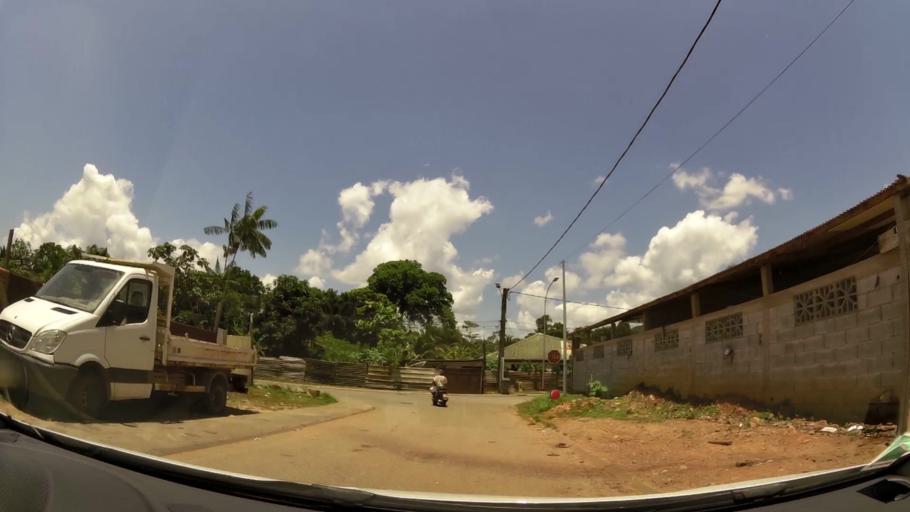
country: GF
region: Guyane
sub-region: Guyane
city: Matoury
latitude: 4.8807
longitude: -52.3423
